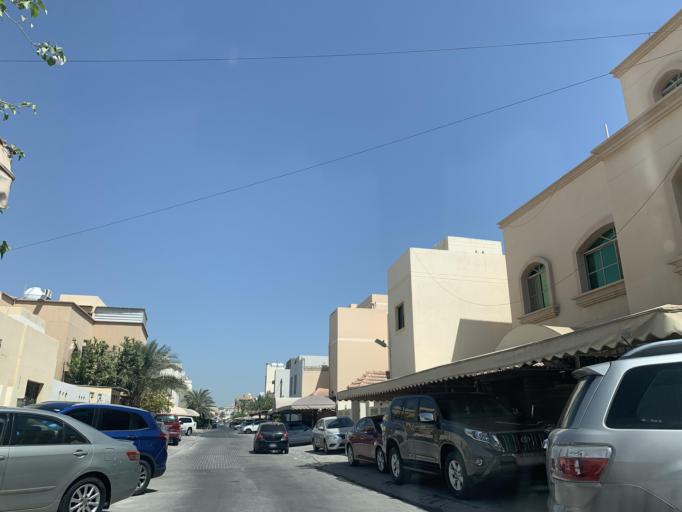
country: BH
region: Northern
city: Ar Rifa'
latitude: 26.1355
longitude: 50.5780
